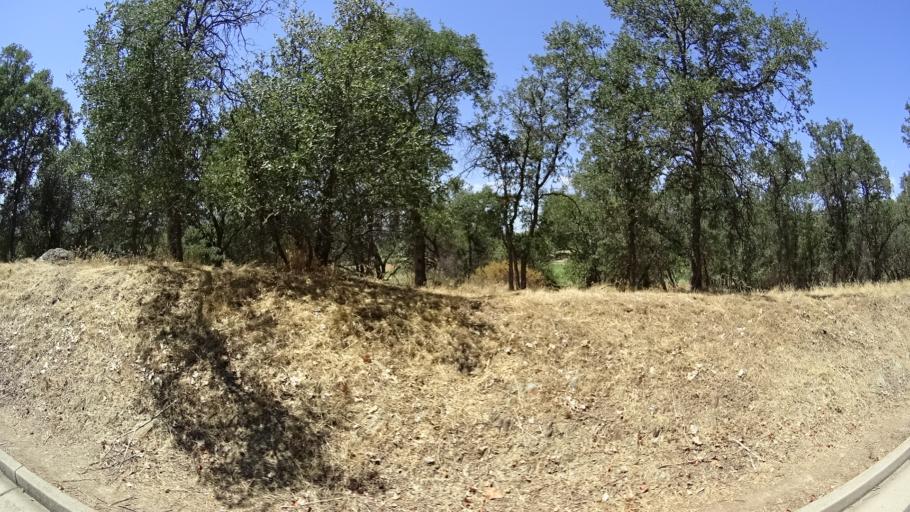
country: US
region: California
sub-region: Calaveras County
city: Angels Camp
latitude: 38.0665
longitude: -120.5510
